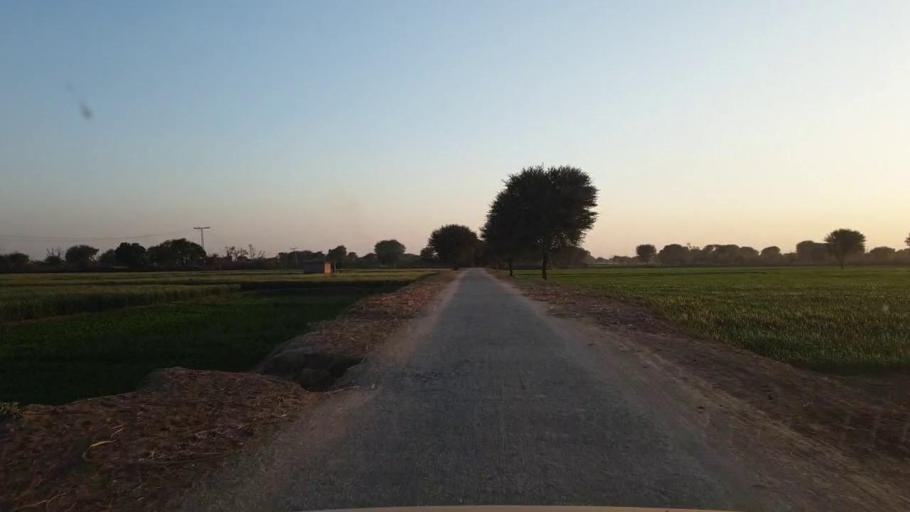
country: PK
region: Sindh
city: Tando Jam
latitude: 25.3055
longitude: 68.6380
